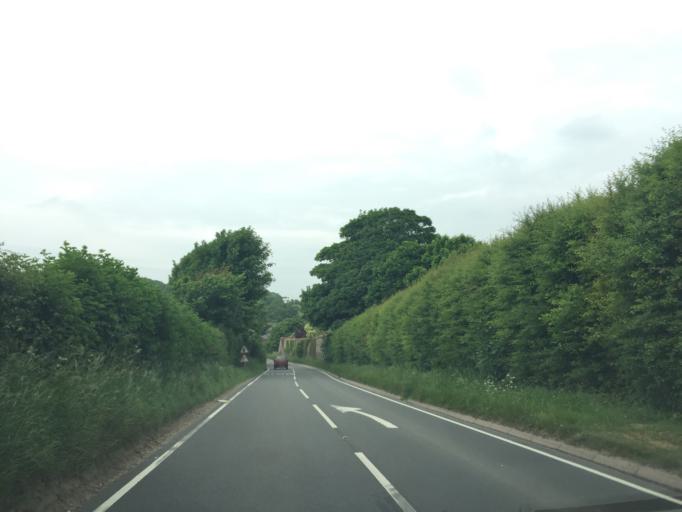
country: GB
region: England
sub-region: Dorset
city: Dorchester
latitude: 50.6913
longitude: -2.4014
